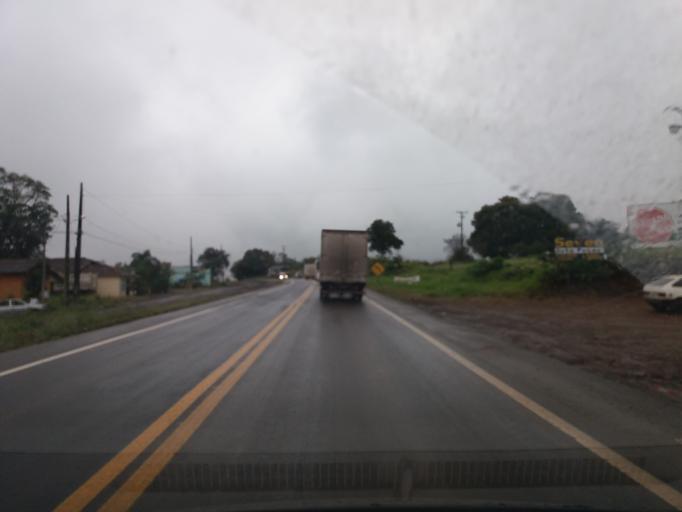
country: BR
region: Parana
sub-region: Realeza
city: Realeza
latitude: -25.4912
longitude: -53.5953
